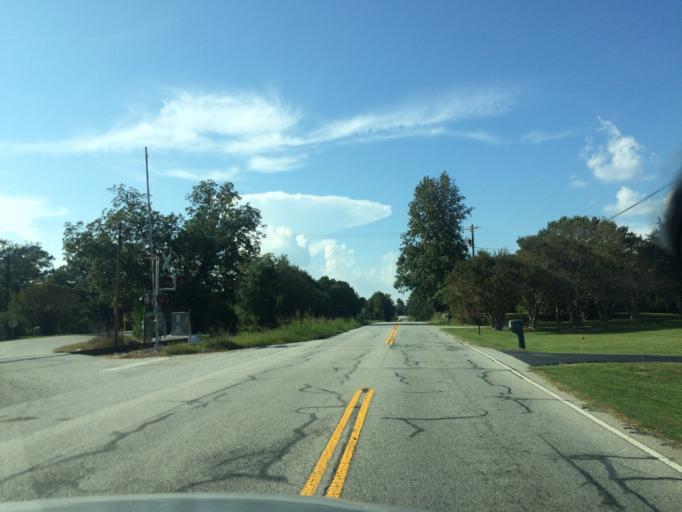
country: US
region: South Carolina
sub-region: Laurens County
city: Laurens
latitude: 34.5750
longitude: -82.0916
